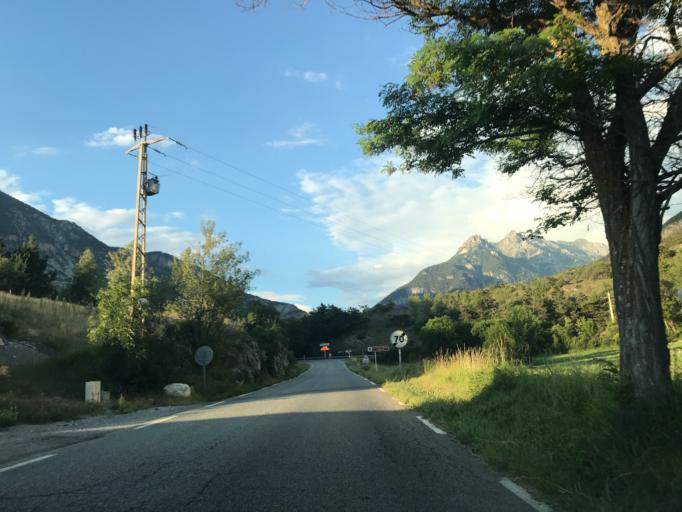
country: FR
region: Provence-Alpes-Cote d'Azur
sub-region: Departement des Hautes-Alpes
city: Guillestre
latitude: 44.6632
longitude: 6.6616
